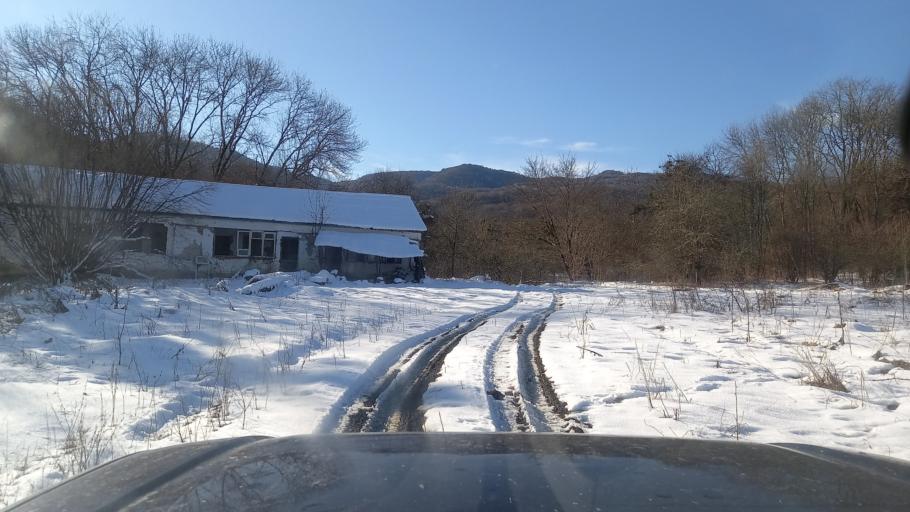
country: RU
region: Adygeya
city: Kamennomostskiy
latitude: 44.2051
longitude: 40.1423
